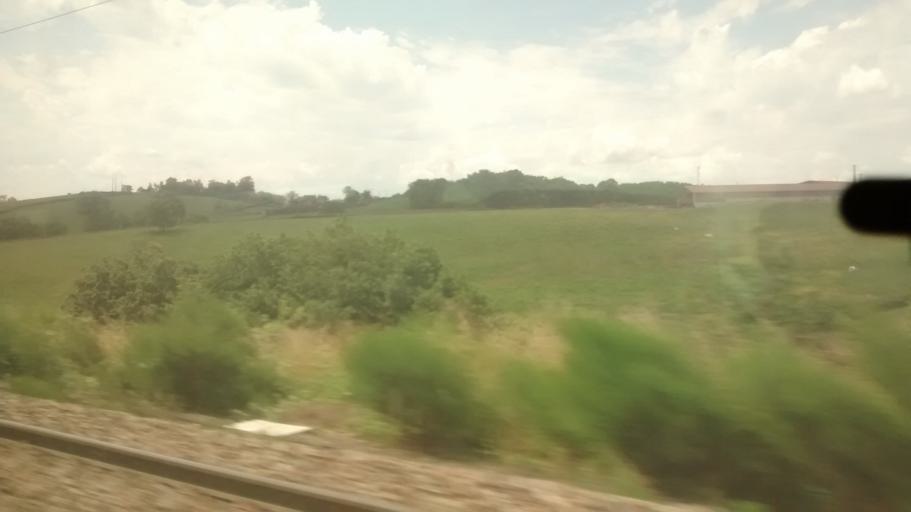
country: FR
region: Bourgogne
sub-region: Departement de Saone-et-Loire
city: Le Breuil
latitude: 46.7900
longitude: 4.4974
